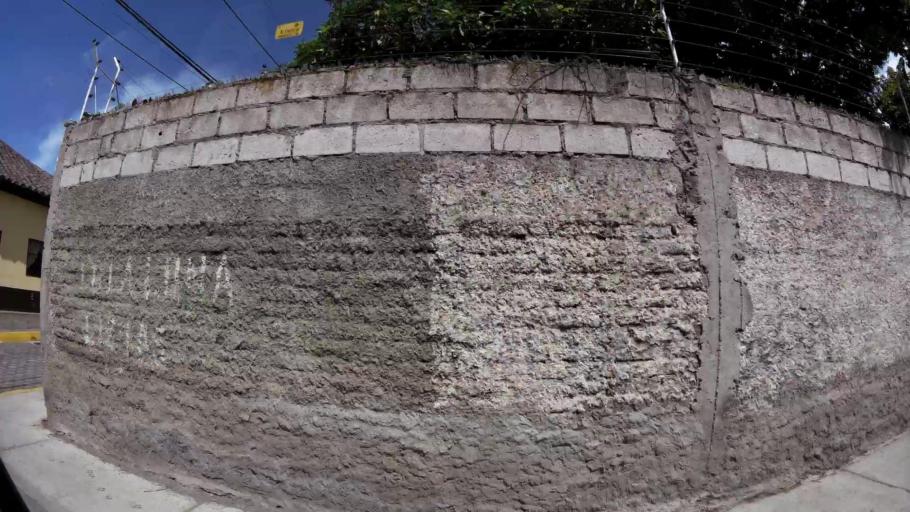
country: EC
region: Chimborazo
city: Guano
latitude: -1.5676
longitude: -78.5308
